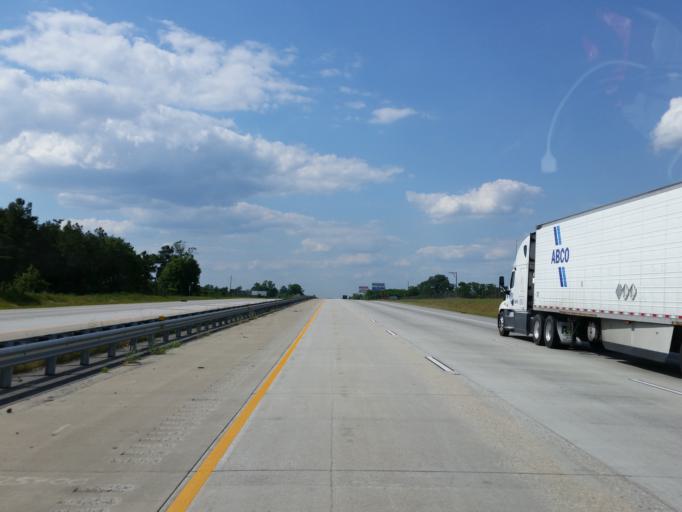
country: US
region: Georgia
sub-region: Dooly County
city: Unadilla
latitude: 32.2797
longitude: -83.7555
